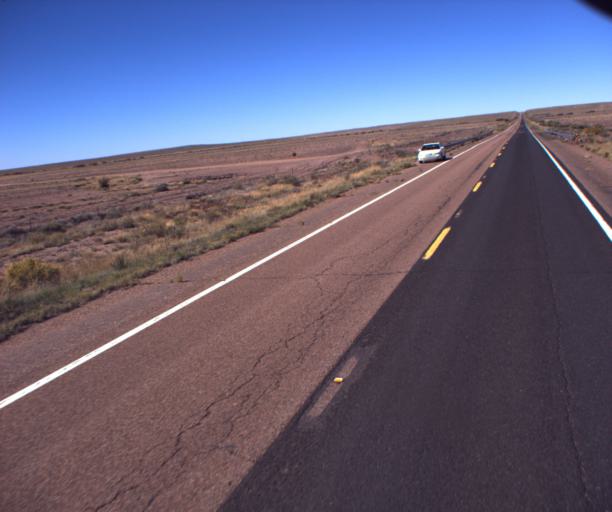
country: US
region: Arizona
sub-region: Navajo County
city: Snowflake
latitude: 34.7339
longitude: -109.7855
